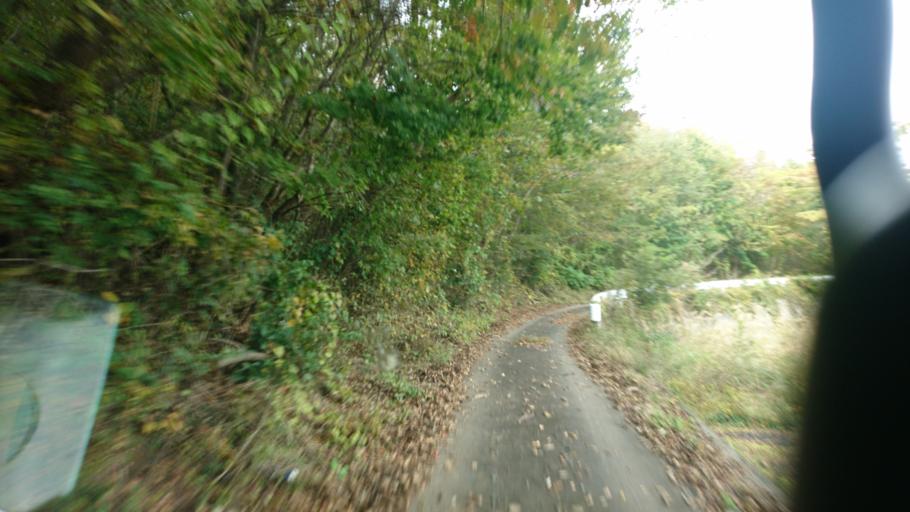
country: JP
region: Gunma
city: Omamacho-omama
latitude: 36.6118
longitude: 139.2463
